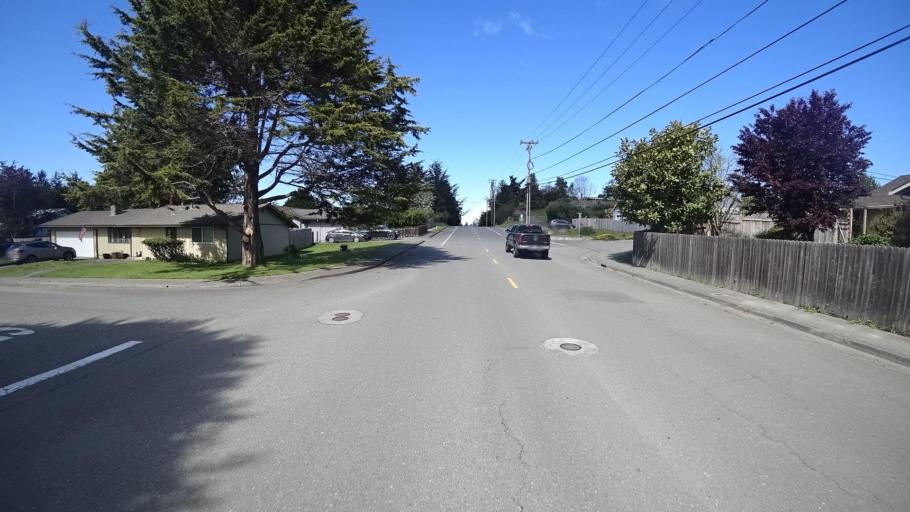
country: US
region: California
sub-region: Humboldt County
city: McKinleyville
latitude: 40.9343
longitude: -124.0833
